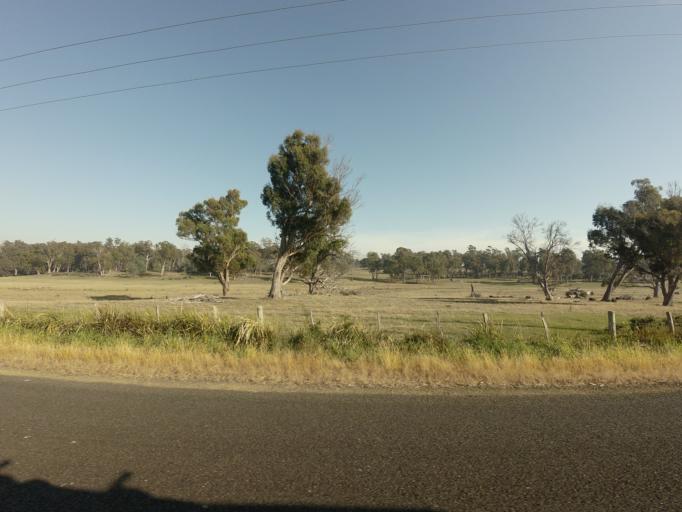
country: AU
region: Tasmania
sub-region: Northern Midlands
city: Longford
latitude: -41.5489
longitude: 146.9912
